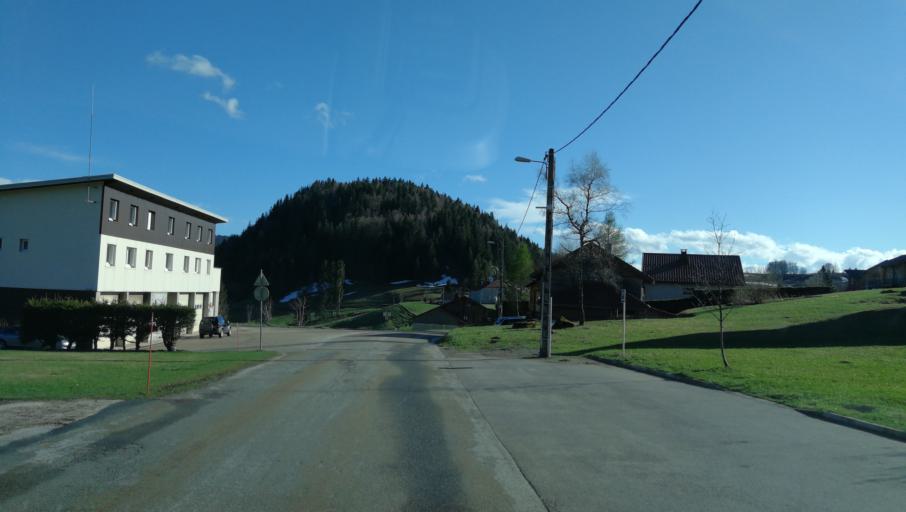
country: FR
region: Franche-Comte
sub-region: Departement du Jura
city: Saint-Claude
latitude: 46.2834
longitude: 5.8468
